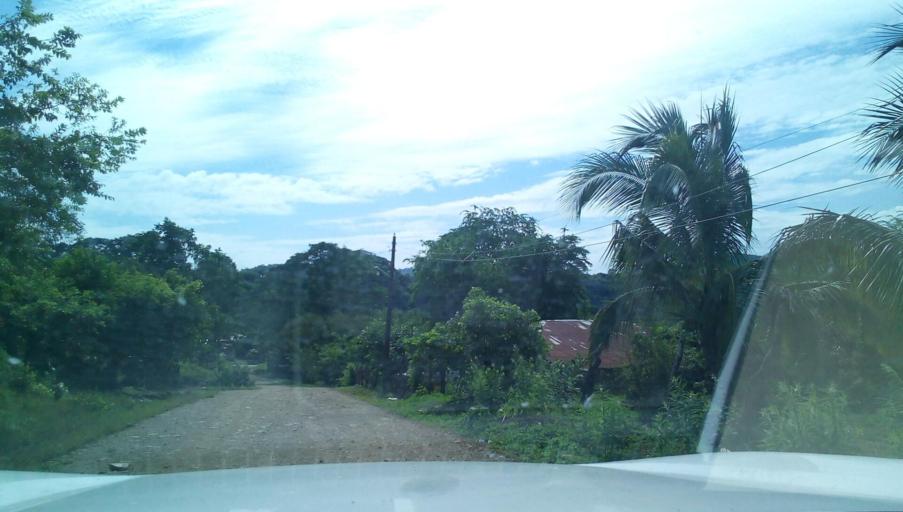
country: MX
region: Veracruz
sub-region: Alamo Temapache
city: Vegas de la Soledad y Soledad Dos
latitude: 20.8975
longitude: -97.9478
